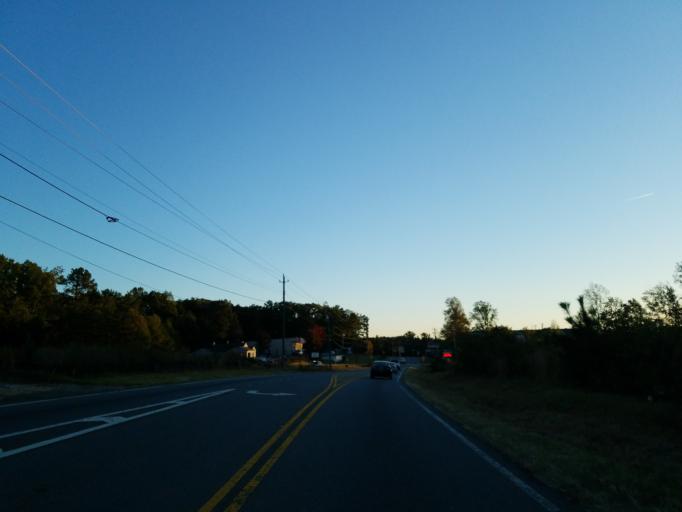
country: US
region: Georgia
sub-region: Forsyth County
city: Cumming
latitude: 34.1846
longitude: -84.1459
